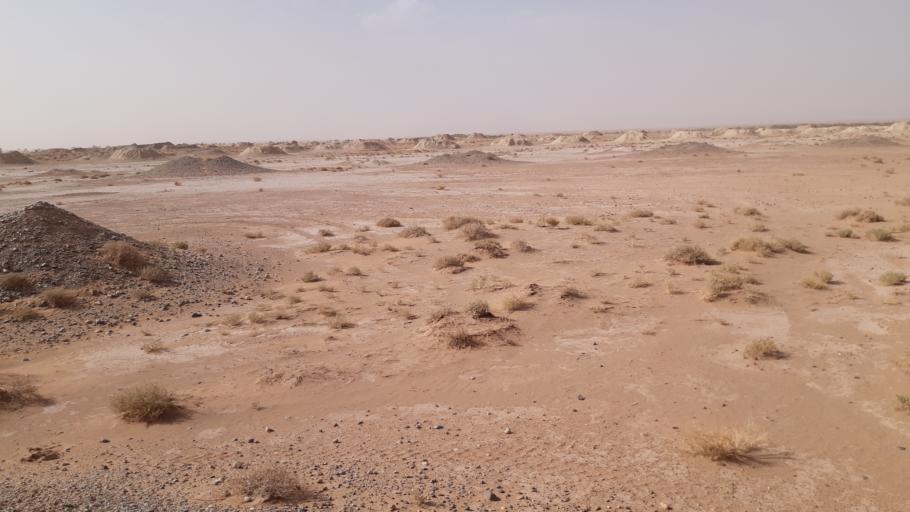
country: MA
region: Meknes-Tafilalet
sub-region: Errachidia
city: Fezna
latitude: 31.5309
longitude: -4.4993
